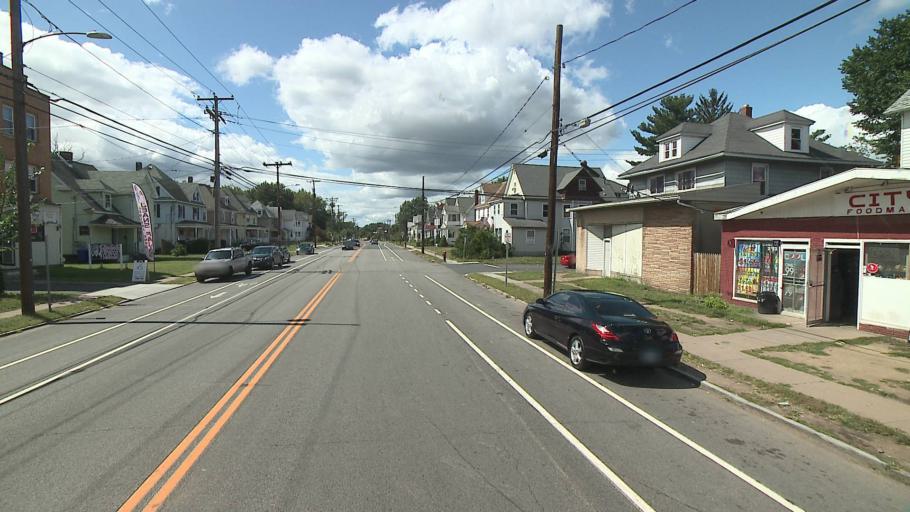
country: US
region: Connecticut
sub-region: Hartford County
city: East Hartford
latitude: 41.7781
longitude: -72.6209
